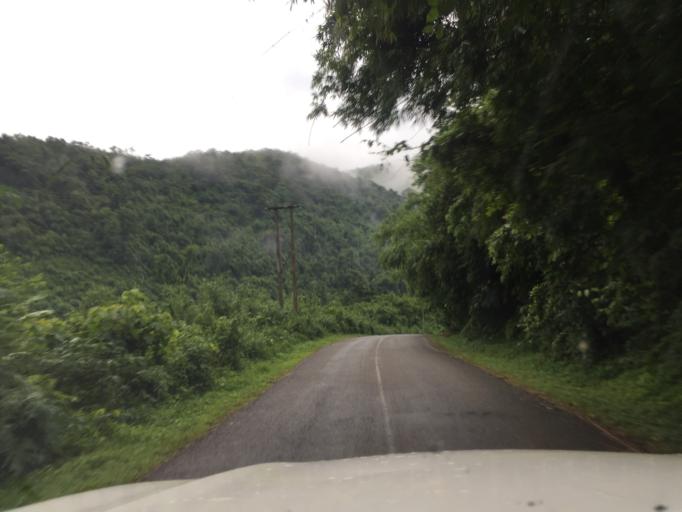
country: LA
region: Oudomxai
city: Muang La
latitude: 20.9014
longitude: 102.1809
